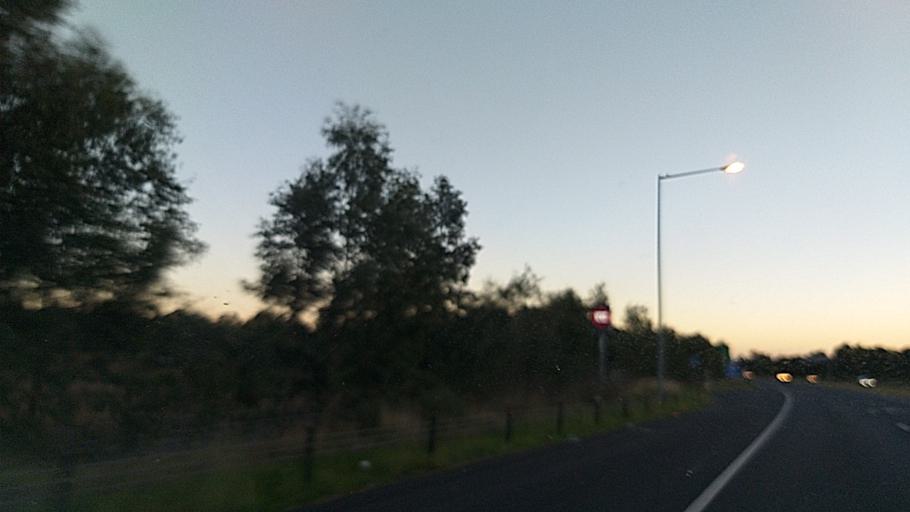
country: AU
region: New South Wales
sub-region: Blacktown
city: Doonside
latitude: -33.7829
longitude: 150.8581
